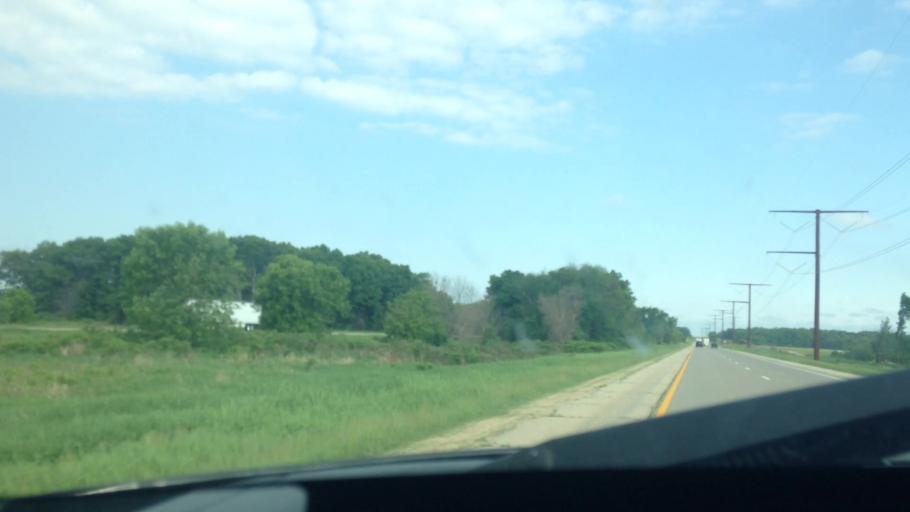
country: US
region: Wisconsin
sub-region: Juneau County
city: Mauston
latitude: 43.8508
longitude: -90.1041
